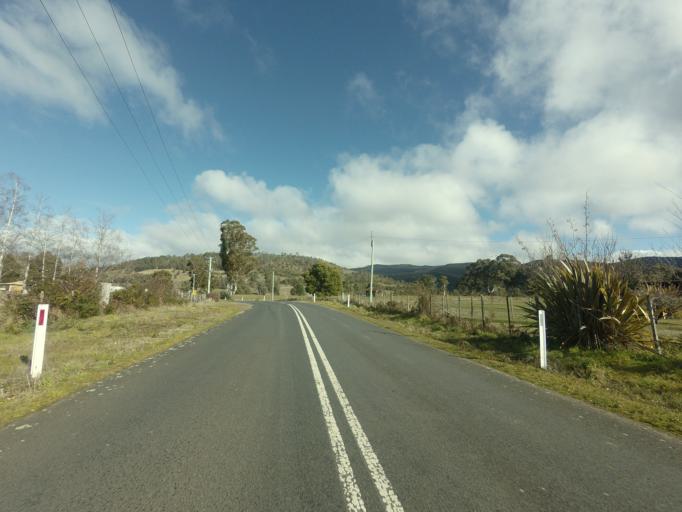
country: AU
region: Tasmania
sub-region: Derwent Valley
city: New Norfolk
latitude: -42.6023
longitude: 146.7063
